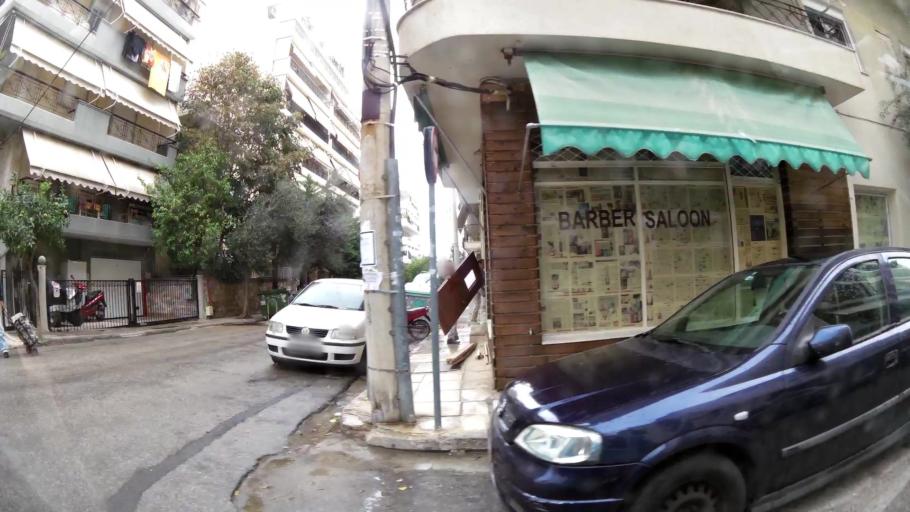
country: GR
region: Attica
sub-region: Nomarchia Athinas
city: Kaisariani
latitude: 37.9665
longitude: 23.7645
